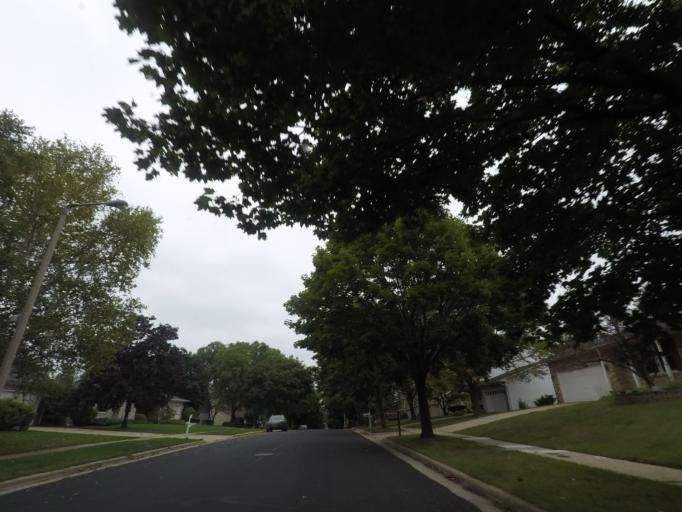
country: US
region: Wisconsin
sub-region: Dane County
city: Middleton
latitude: 43.0682
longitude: -89.5200
